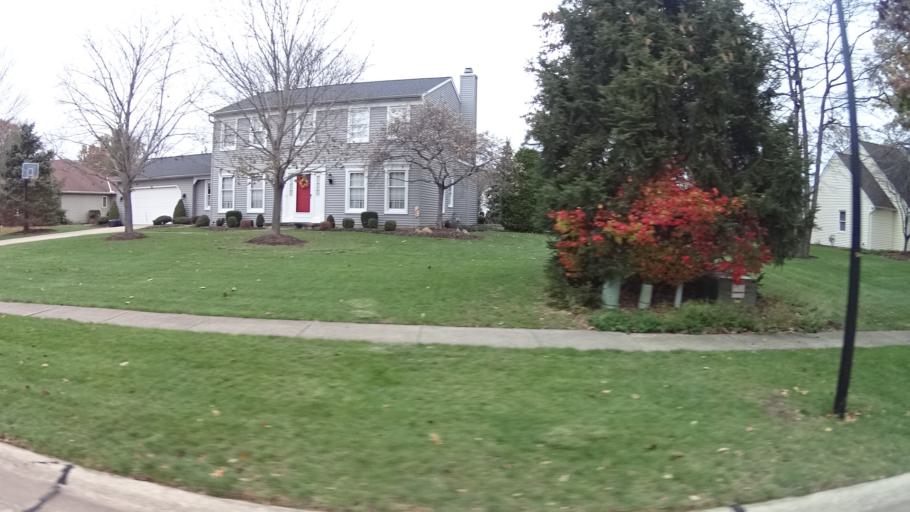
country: US
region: Ohio
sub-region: Lorain County
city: Avon Center
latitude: 41.4872
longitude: -81.9921
